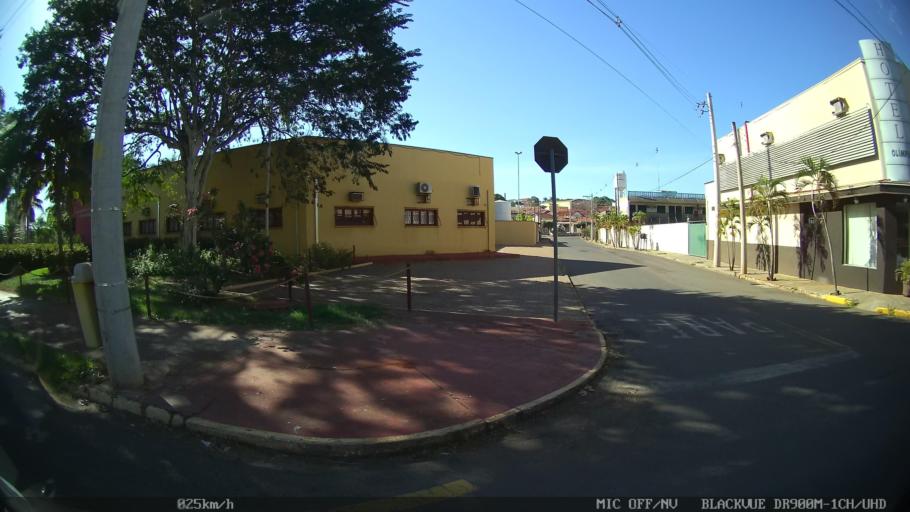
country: BR
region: Sao Paulo
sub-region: Olimpia
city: Olimpia
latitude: -20.7421
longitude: -48.9086
